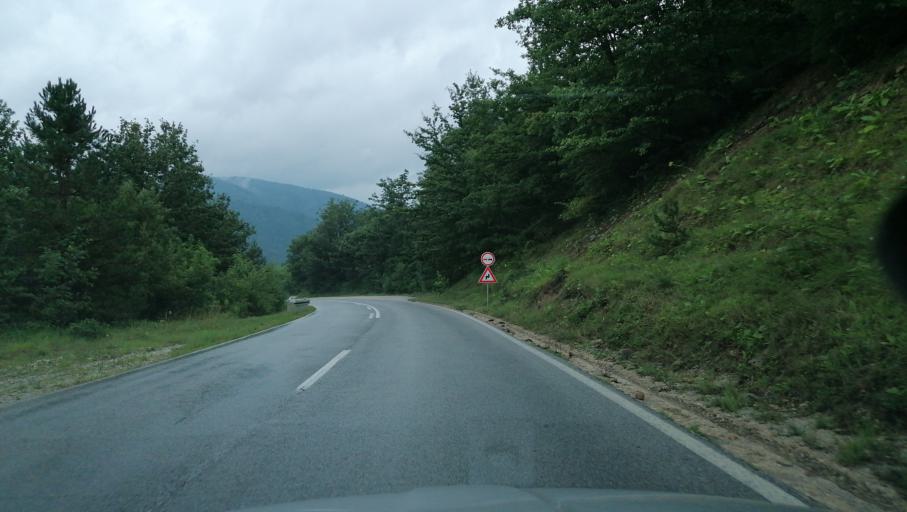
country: RS
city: Durici
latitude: 43.8062
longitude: 19.5107
